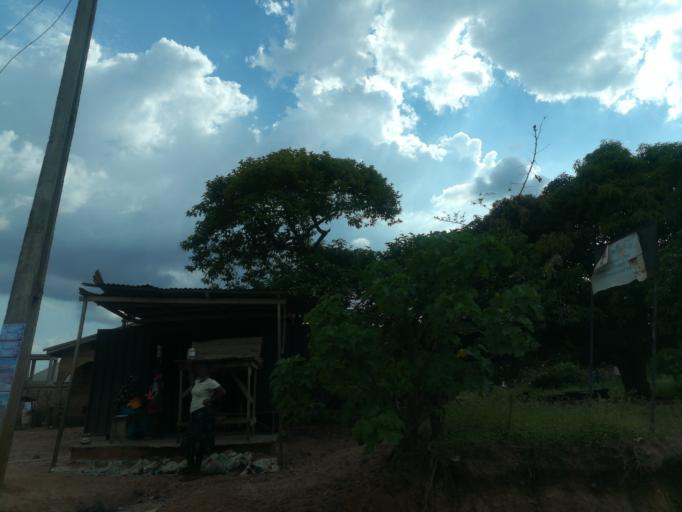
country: NG
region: Oyo
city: Ibadan
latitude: 7.4087
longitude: 3.8256
